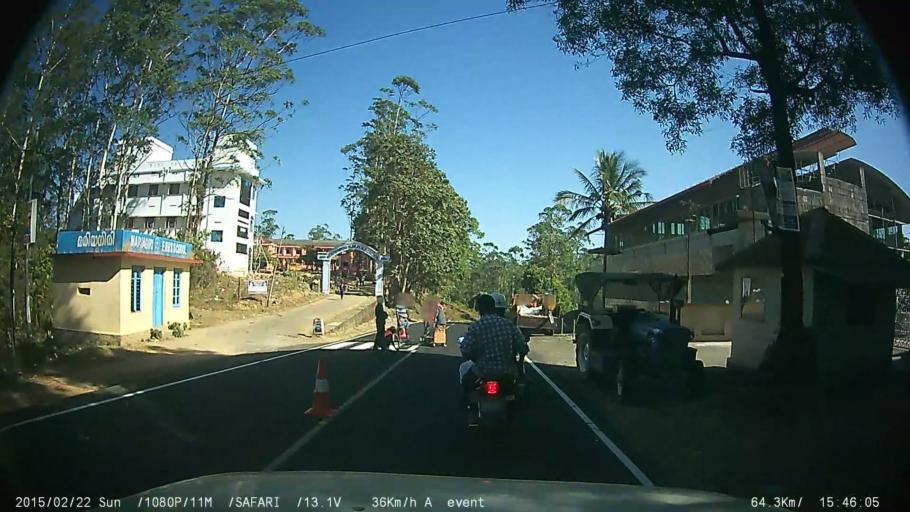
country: IN
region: Kerala
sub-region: Kottayam
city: Erattupetta
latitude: 9.5804
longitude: 76.9821
